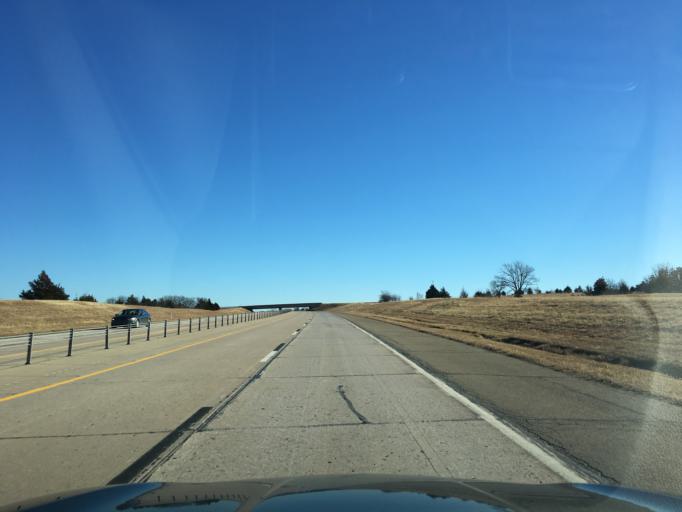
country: US
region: Oklahoma
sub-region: Payne County
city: Stillwater
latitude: 36.2438
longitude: -96.9564
